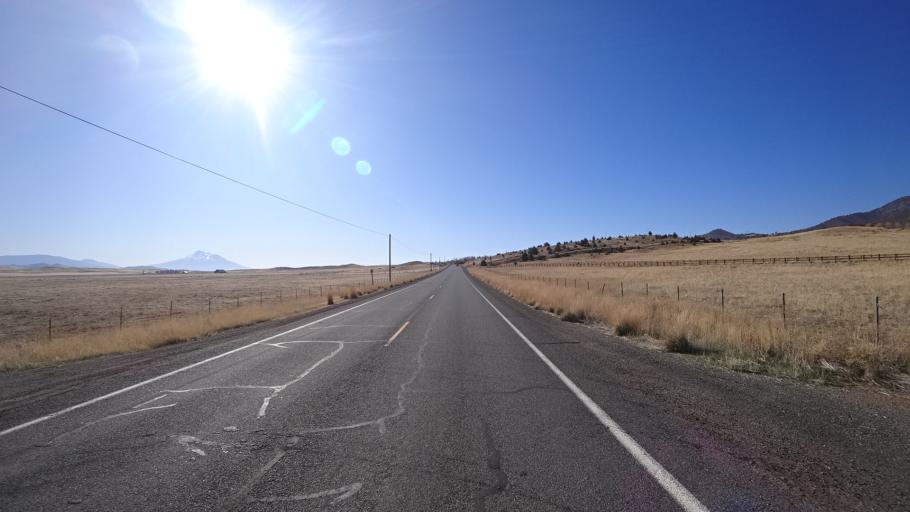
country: US
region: California
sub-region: Siskiyou County
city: Montague
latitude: 41.8249
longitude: -122.4945
